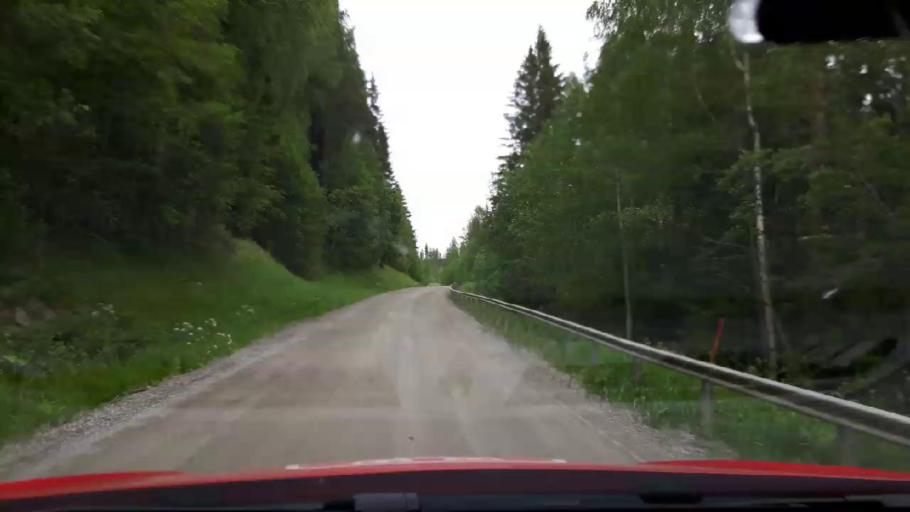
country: SE
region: Jaemtland
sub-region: Ragunda Kommun
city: Hammarstrand
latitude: 63.1866
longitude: 16.1449
